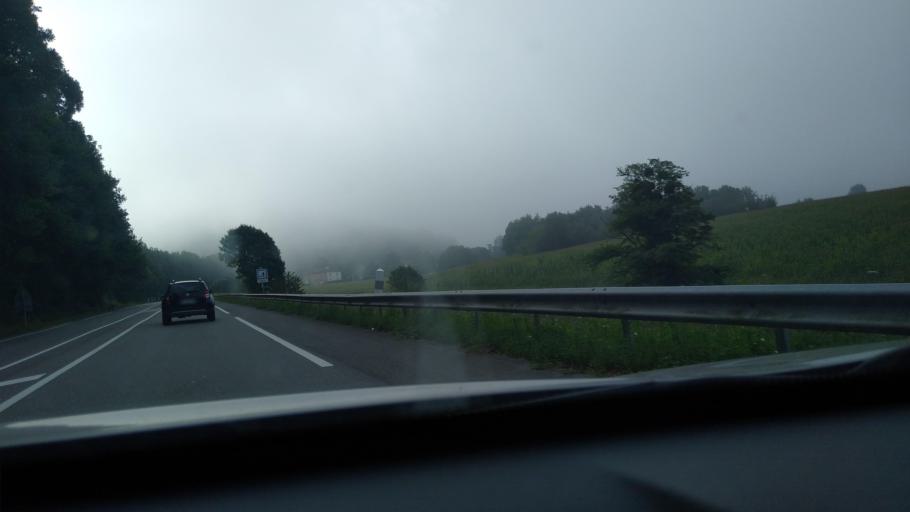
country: FR
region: Midi-Pyrenees
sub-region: Departement de la Haute-Garonne
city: Salies-du-Salat
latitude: 43.1181
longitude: 0.9331
